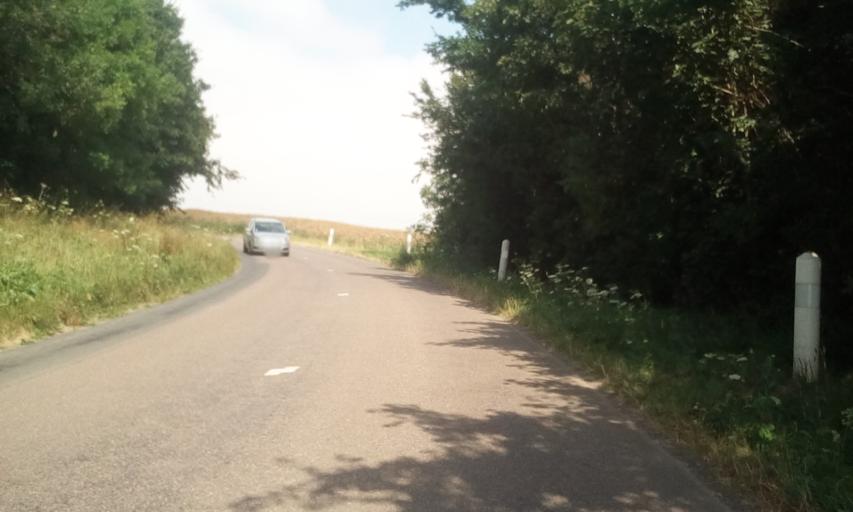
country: FR
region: Lower Normandy
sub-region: Departement du Calvados
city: Douvres-la-Delivrande
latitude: 49.2910
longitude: -0.4121
